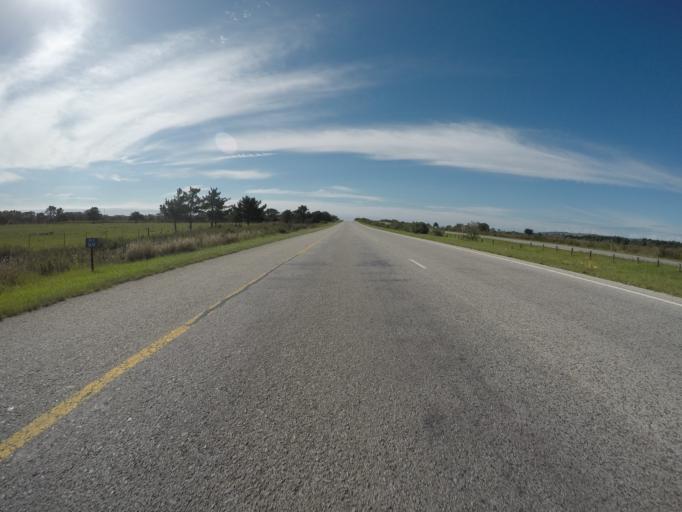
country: ZA
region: Eastern Cape
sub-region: Nelson Mandela Bay Metropolitan Municipality
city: Port Elizabeth
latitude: -33.9495
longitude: 25.4375
